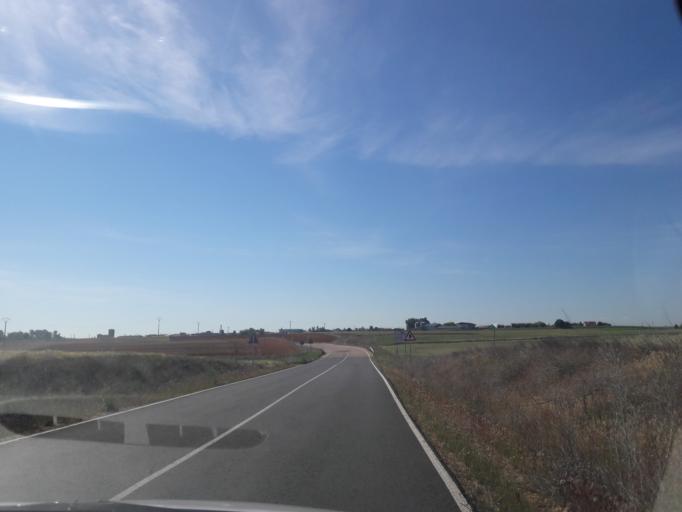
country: ES
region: Castille and Leon
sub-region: Provincia de Salamanca
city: Espino de la Orbada
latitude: 41.0867
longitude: -5.4081
